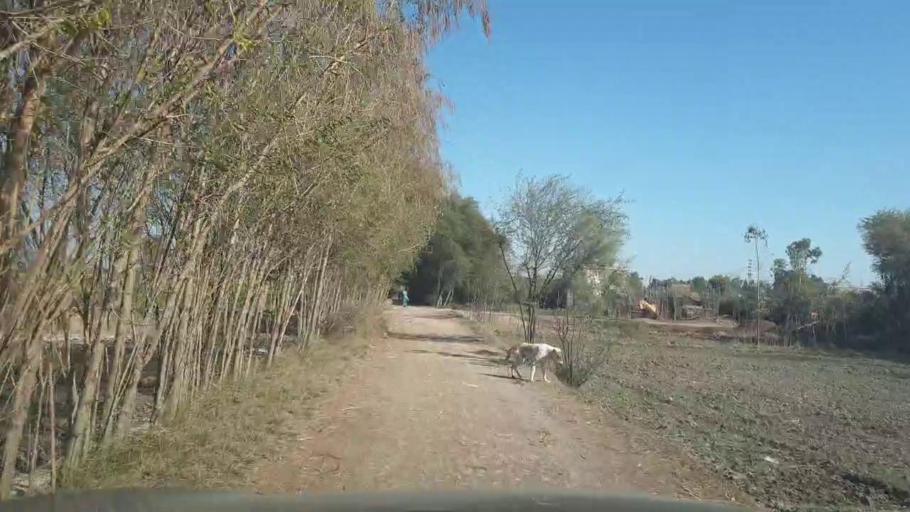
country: PK
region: Sindh
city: Mirpur Mathelo
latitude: 28.0779
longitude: 69.4907
